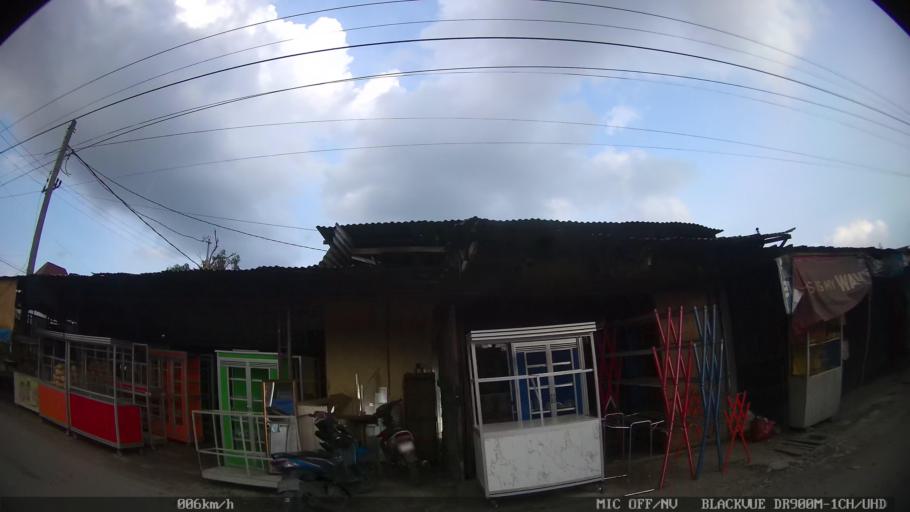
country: ID
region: North Sumatra
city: Medan
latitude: 3.5865
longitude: 98.7408
